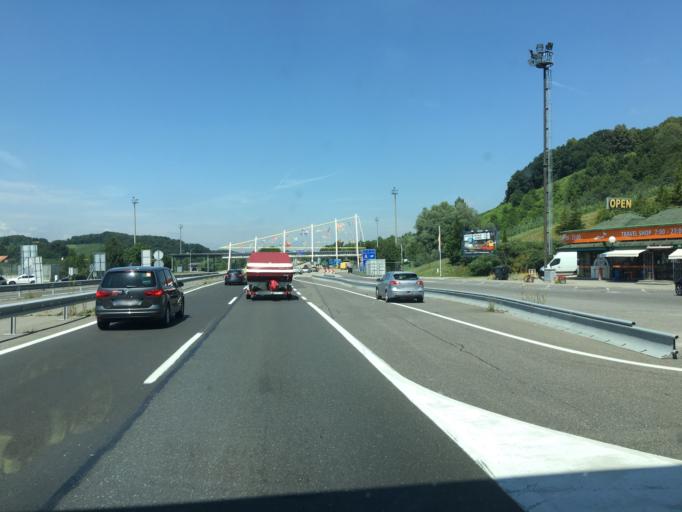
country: SI
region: Sentilj
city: Sentilj v Slov. Goricah
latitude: 46.6902
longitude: 15.6460
